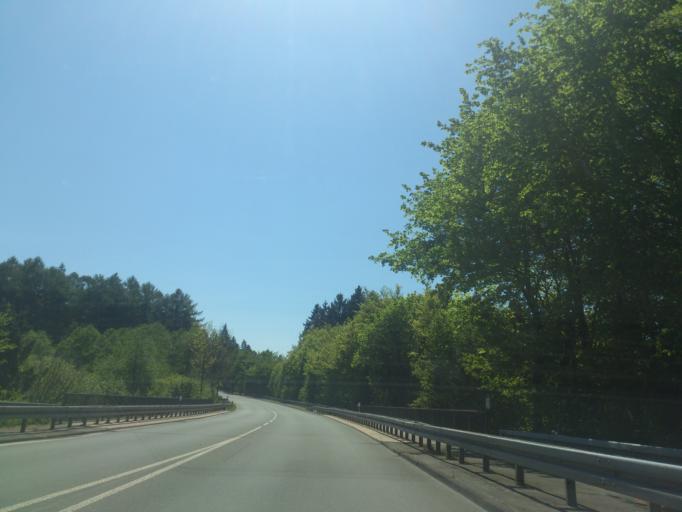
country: DE
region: North Rhine-Westphalia
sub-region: Regierungsbezirk Detmold
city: Bad Driburg
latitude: 51.6789
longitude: 8.9644
